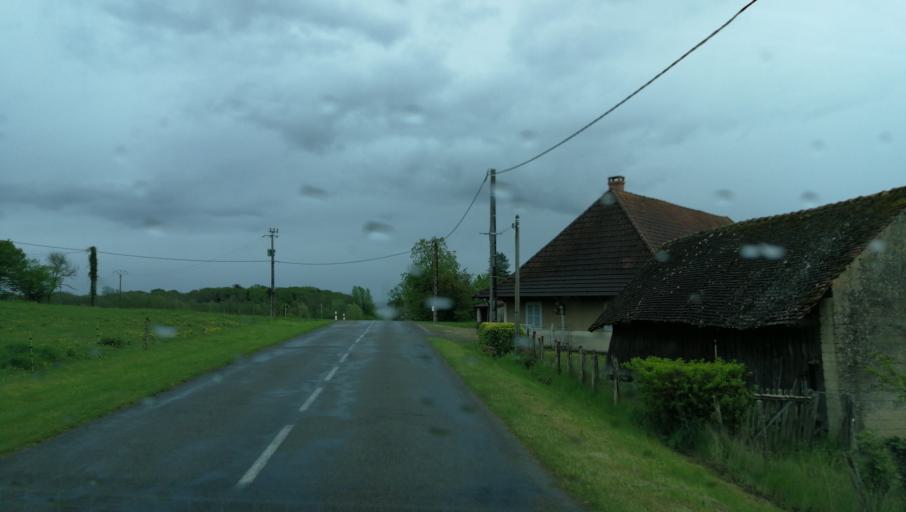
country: FR
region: Franche-Comte
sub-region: Departement du Jura
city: Bletterans
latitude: 46.7814
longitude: 5.4184
